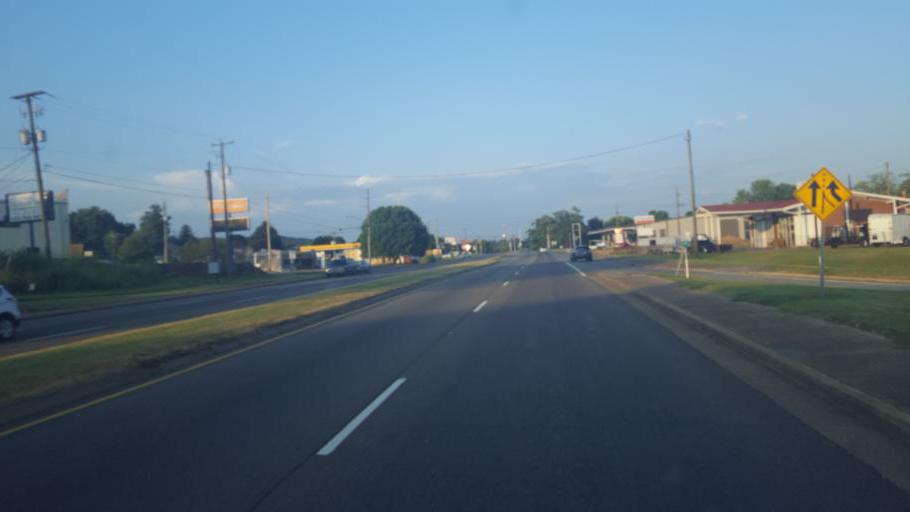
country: US
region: Tennessee
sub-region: Sullivan County
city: Kingsport
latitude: 36.5571
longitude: -82.5798
